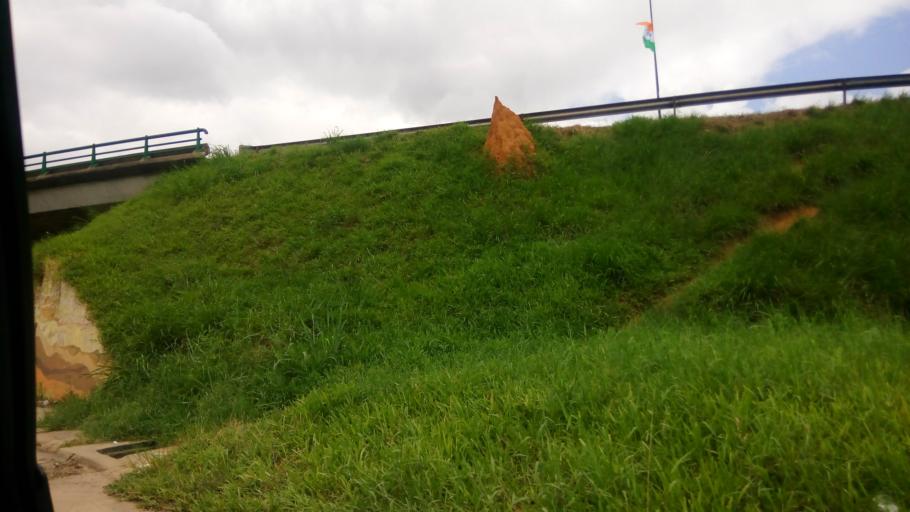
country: CI
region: Lagunes
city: Abidjan
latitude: 5.3409
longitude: -4.0163
